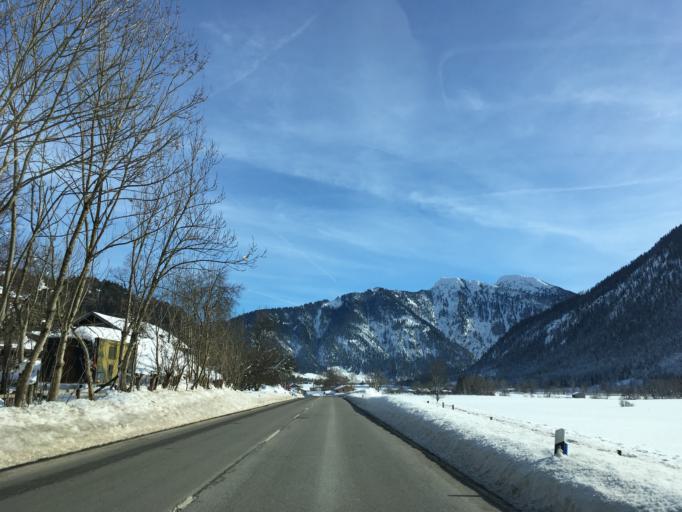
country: DE
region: Bavaria
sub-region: Upper Bavaria
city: Bayrischzell
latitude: 47.6855
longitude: 11.9850
